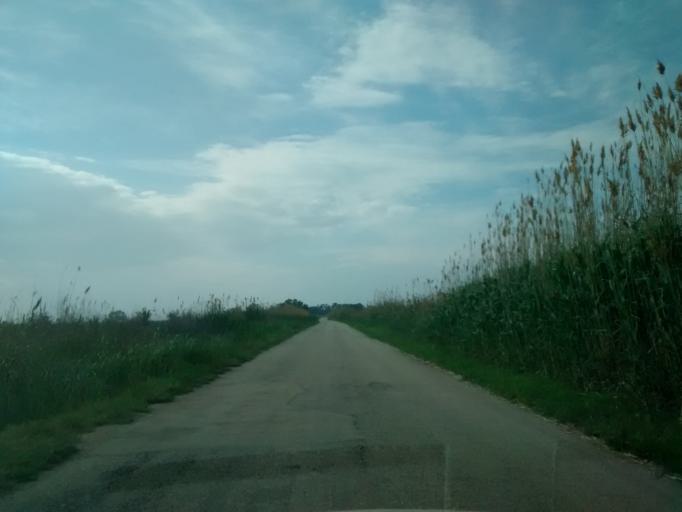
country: ES
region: Catalonia
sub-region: Provincia de Tarragona
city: Deltebre
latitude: 40.6923
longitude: 0.8419
